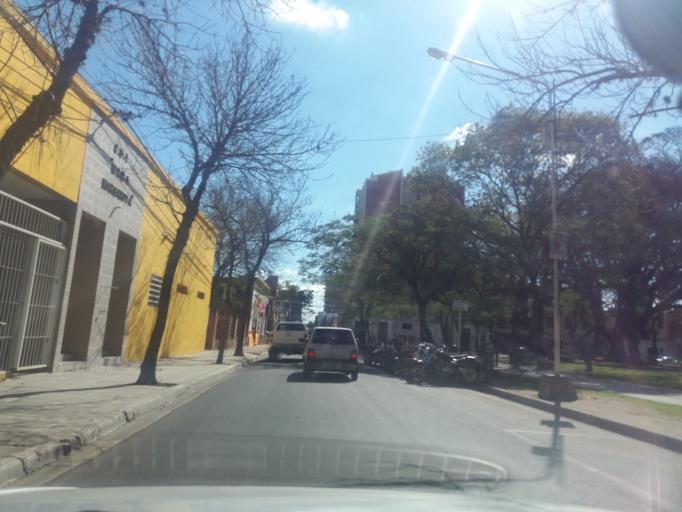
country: AR
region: Corrientes
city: Corrientes
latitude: -27.4719
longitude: -58.8335
